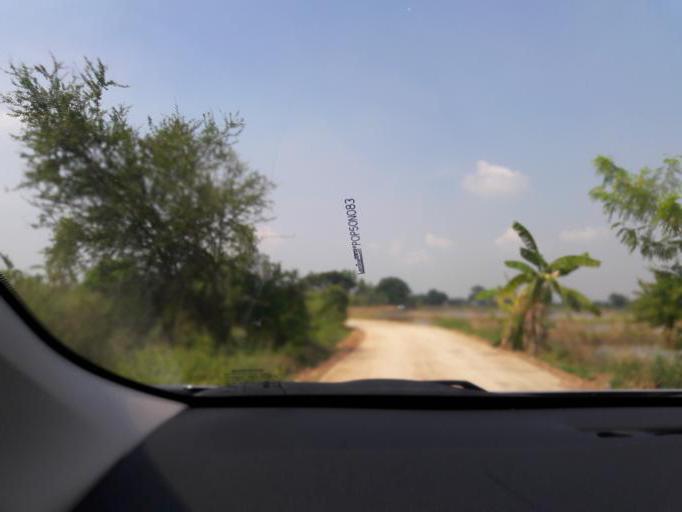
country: TH
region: Ang Thong
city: Ang Thong
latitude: 14.5608
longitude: 100.4212
